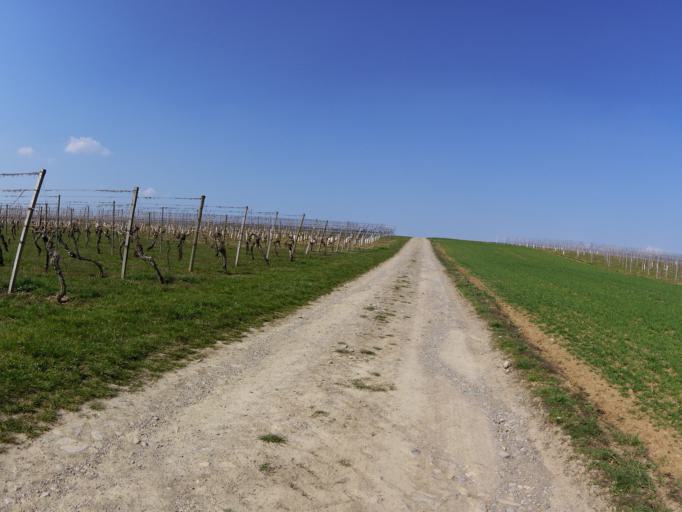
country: DE
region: Bavaria
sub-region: Regierungsbezirk Unterfranken
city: Mainstockheim
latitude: 49.7881
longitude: 10.1380
